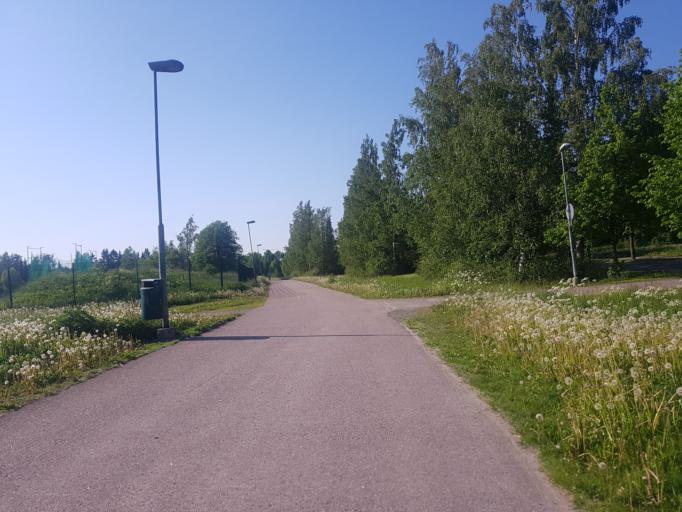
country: FI
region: Uusimaa
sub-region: Helsinki
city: Vantaa
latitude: 60.2499
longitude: 24.9960
